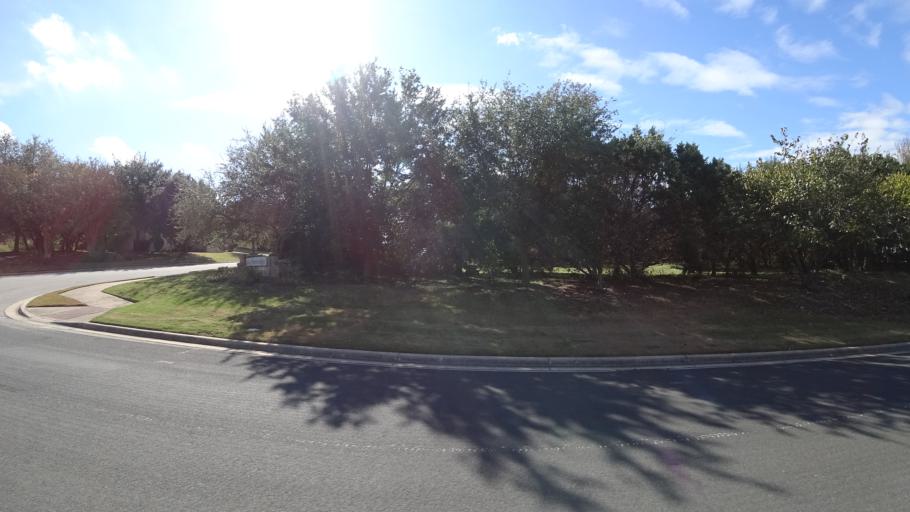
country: US
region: Texas
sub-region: Travis County
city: Hudson Bend
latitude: 30.3807
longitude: -97.9075
